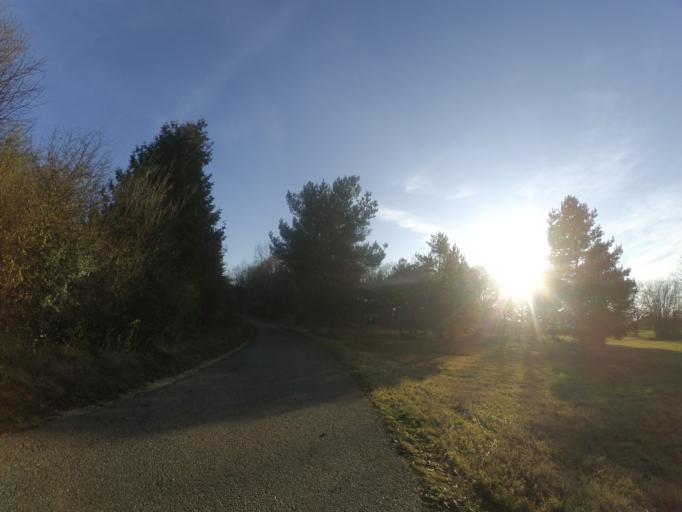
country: DE
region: Baden-Wuerttemberg
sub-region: Tuebingen Region
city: Dornstadt
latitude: 48.4399
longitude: 9.8968
